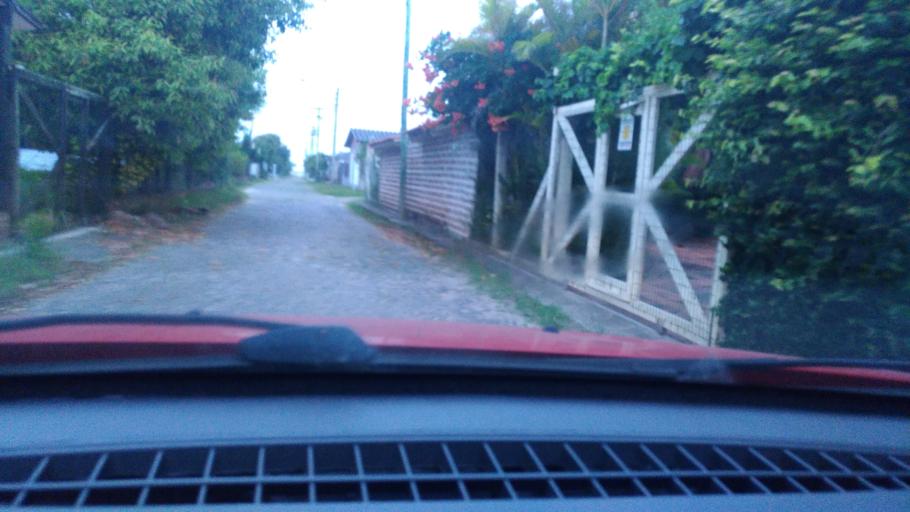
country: BR
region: Rio Grande do Sul
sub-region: Capao Da Canoa
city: Capao da Canoa
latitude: -29.8485
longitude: -50.0633
